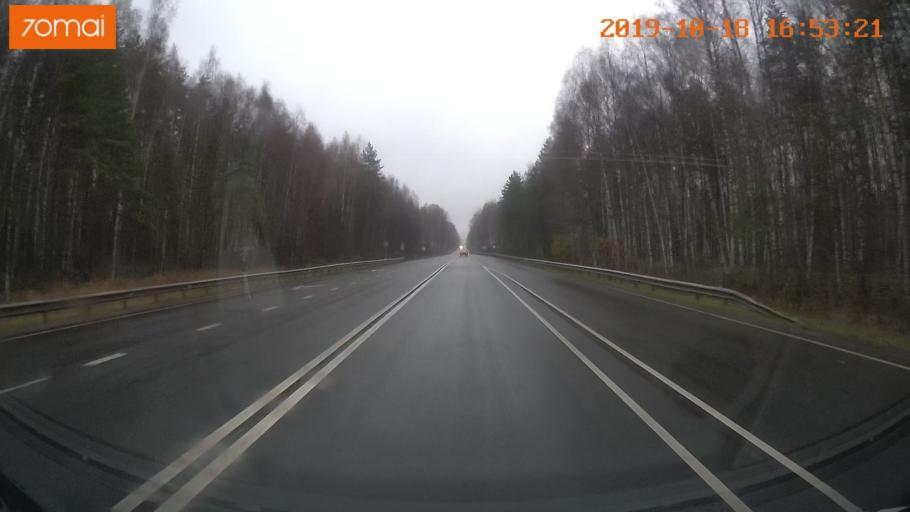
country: RU
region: Ivanovo
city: Nerl'
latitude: 56.6137
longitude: 40.5594
